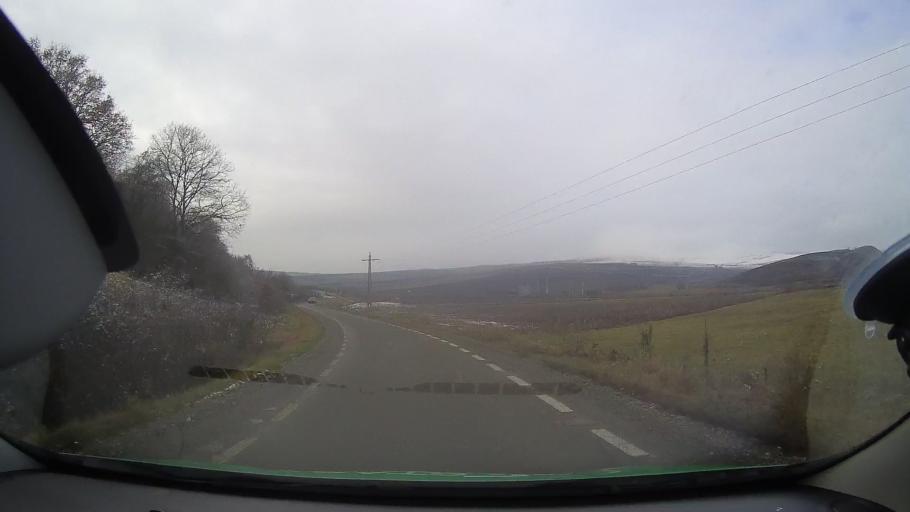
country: RO
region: Mures
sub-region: Comuna Atintis
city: Atintis
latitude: 46.4107
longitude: 24.0830
